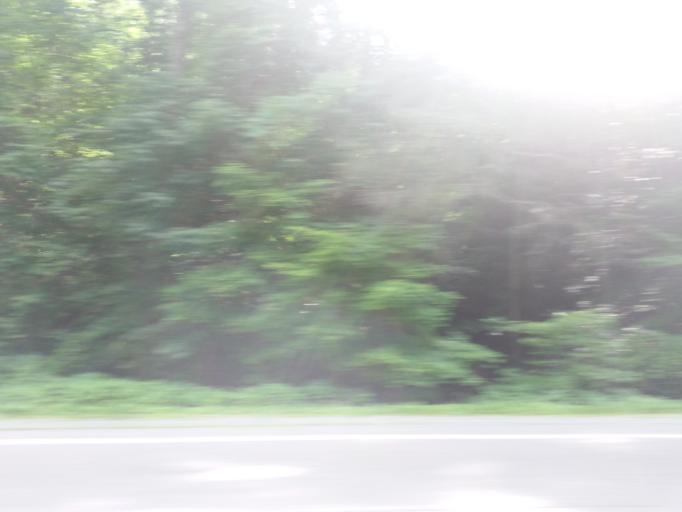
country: US
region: Virginia
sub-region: Lee County
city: Pennington Gap
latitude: 36.7634
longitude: -83.0892
